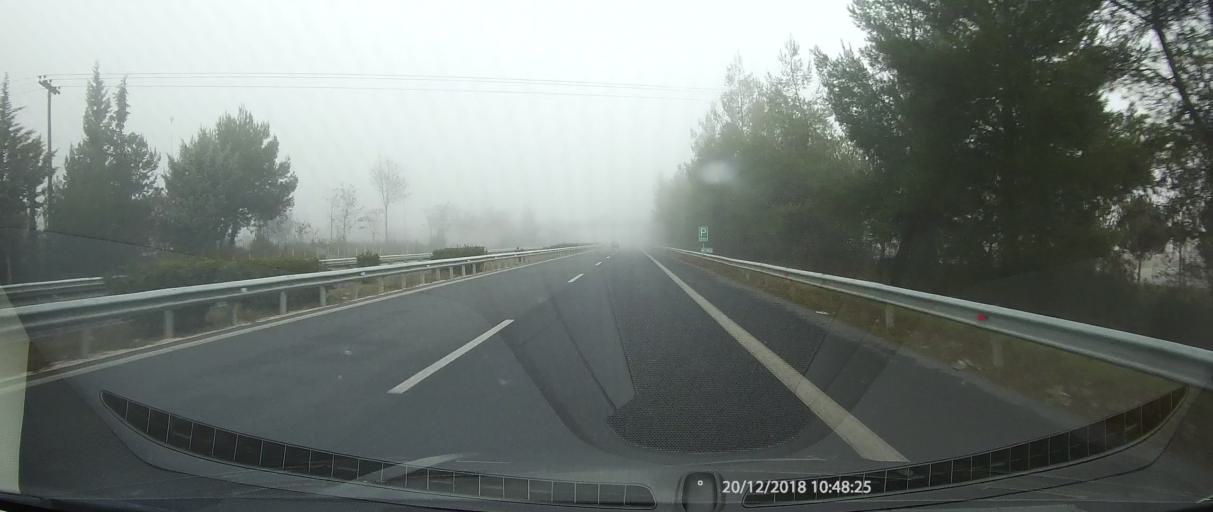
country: GR
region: Peloponnese
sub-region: Nomos Arkadias
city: Tripoli
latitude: 37.5160
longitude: 22.4057
